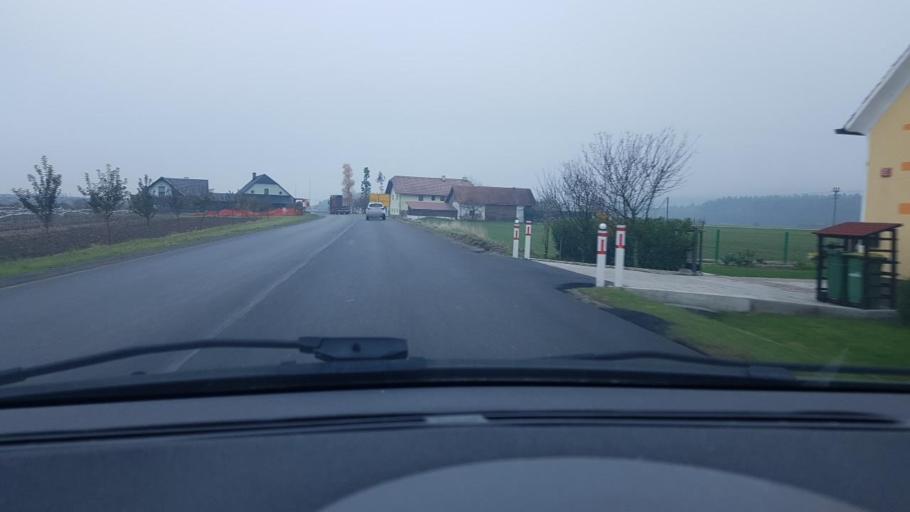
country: SI
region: Tabor
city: Tabor
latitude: 46.2477
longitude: 15.0293
